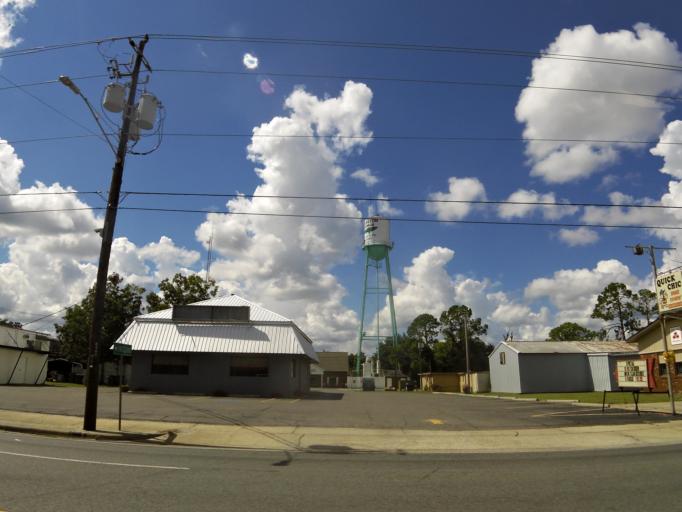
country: US
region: Georgia
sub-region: Charlton County
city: Folkston
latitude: 30.8321
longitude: -82.0062
